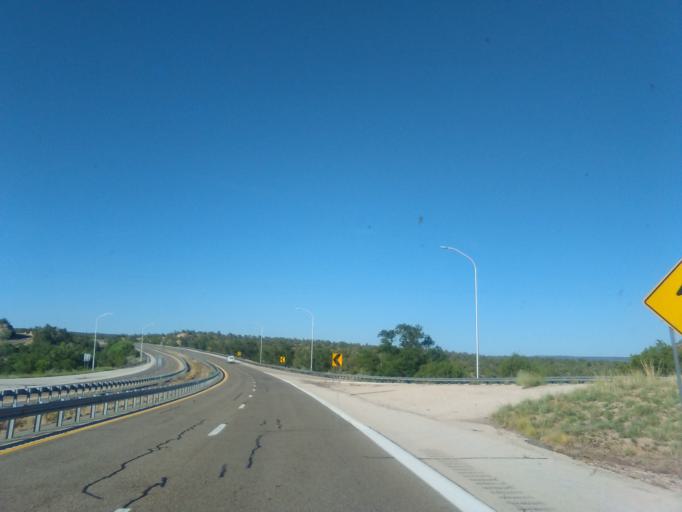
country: US
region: New Mexico
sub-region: San Miguel County
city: Las Vegas
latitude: 35.3958
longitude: -105.3222
